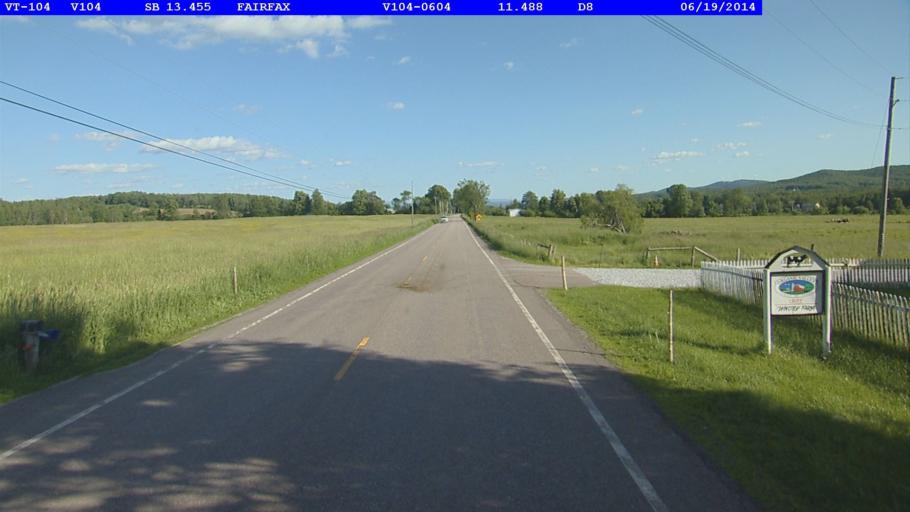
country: US
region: Vermont
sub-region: Franklin County
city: Saint Albans
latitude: 44.7494
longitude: -73.0534
